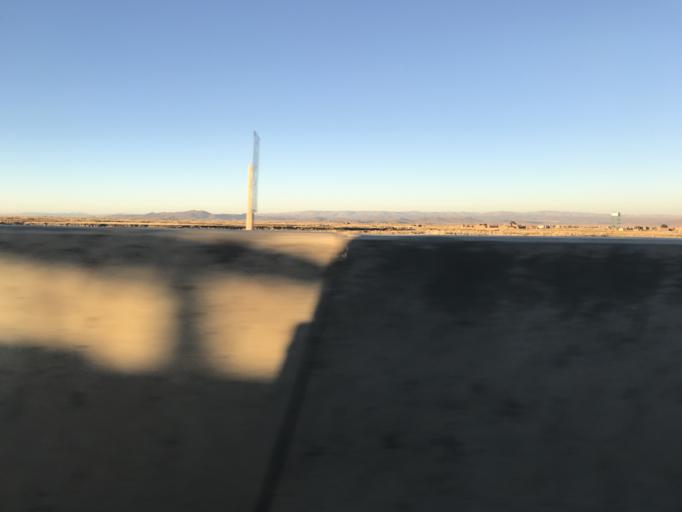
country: BO
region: La Paz
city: Batallas
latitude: -16.3110
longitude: -68.4556
